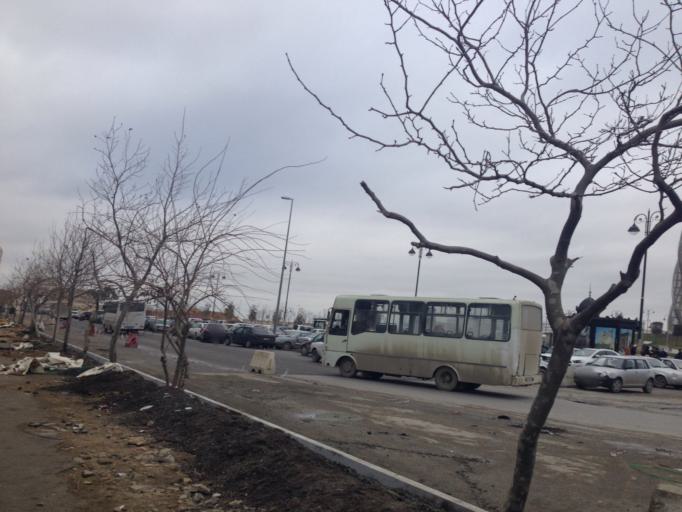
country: AZ
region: Baki
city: Sabuncu
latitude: 40.4209
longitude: 49.9162
